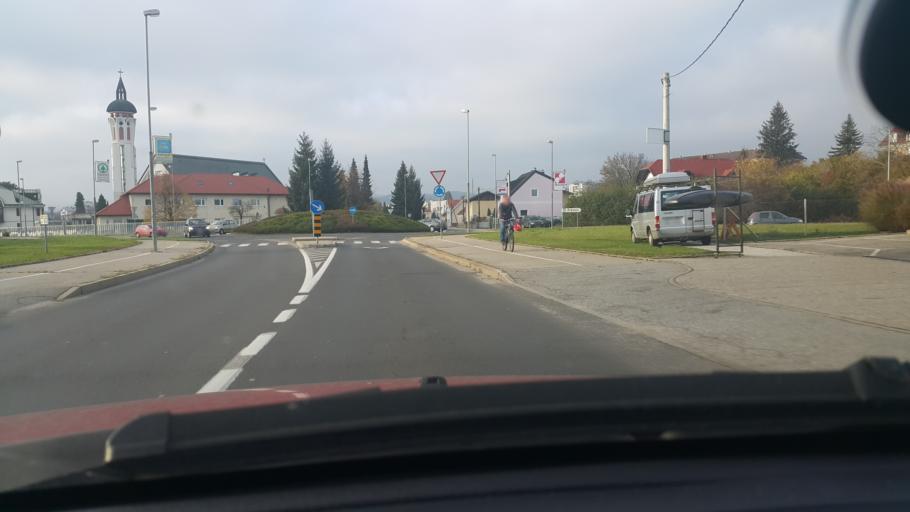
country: SI
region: Maribor
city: Maribor
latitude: 46.5479
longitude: 15.6685
